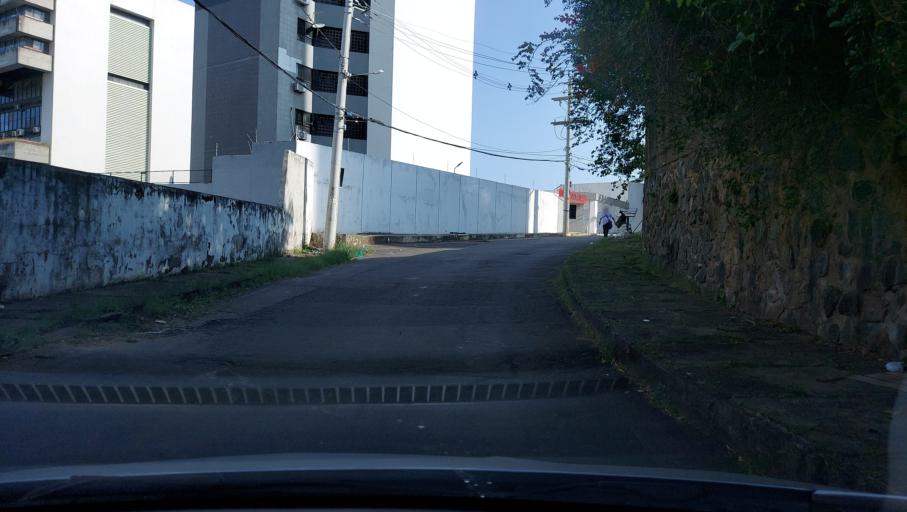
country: BR
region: Bahia
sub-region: Salvador
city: Salvador
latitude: -12.9863
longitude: -38.4681
